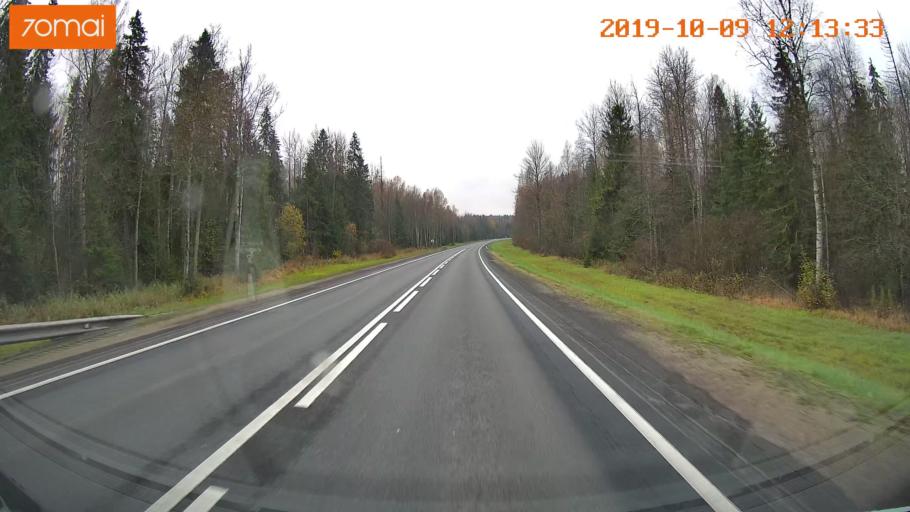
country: RU
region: Jaroslavl
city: Prechistoye
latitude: 58.5088
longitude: 40.3451
